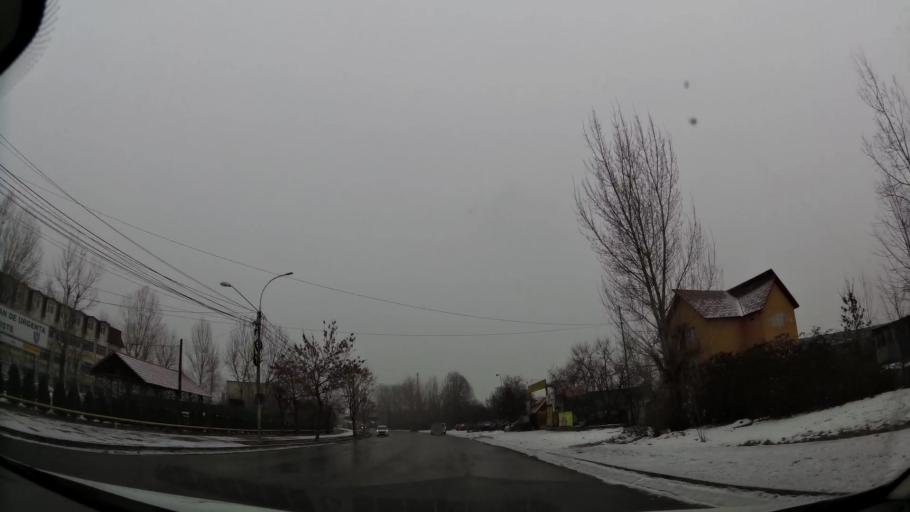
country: RO
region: Dambovita
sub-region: Municipiul Targoviste
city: Targoviste
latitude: 44.9124
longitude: 25.4454
